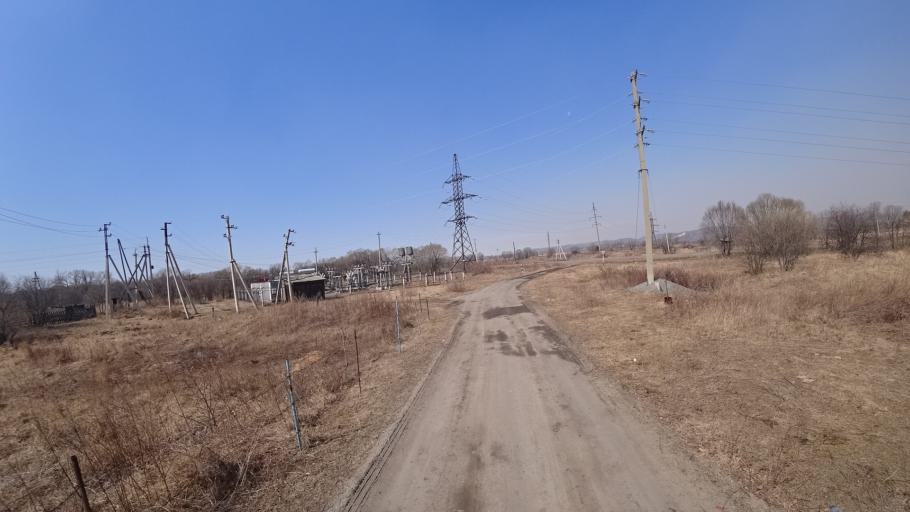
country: RU
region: Amur
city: Novobureyskiy
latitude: 49.7892
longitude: 129.8399
